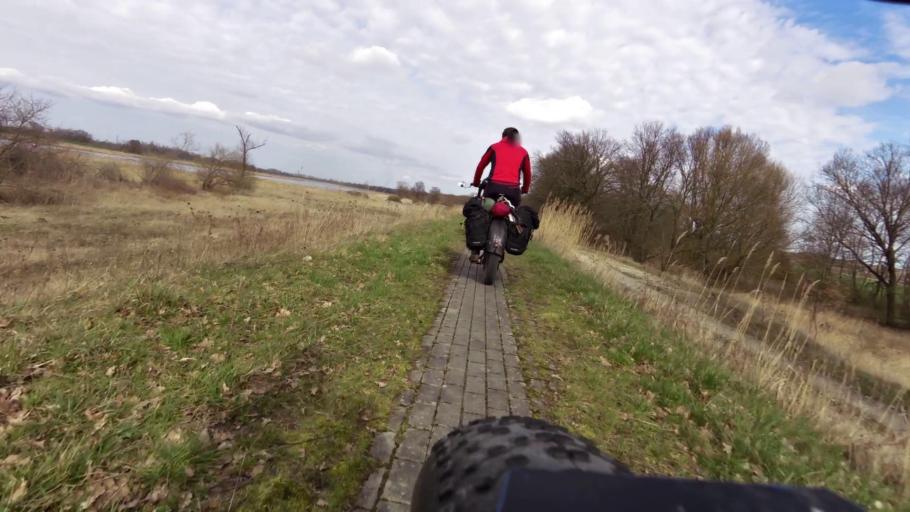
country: PL
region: Lubusz
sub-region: Powiat slubicki
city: Gorzyca
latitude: 52.4787
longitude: 14.6219
